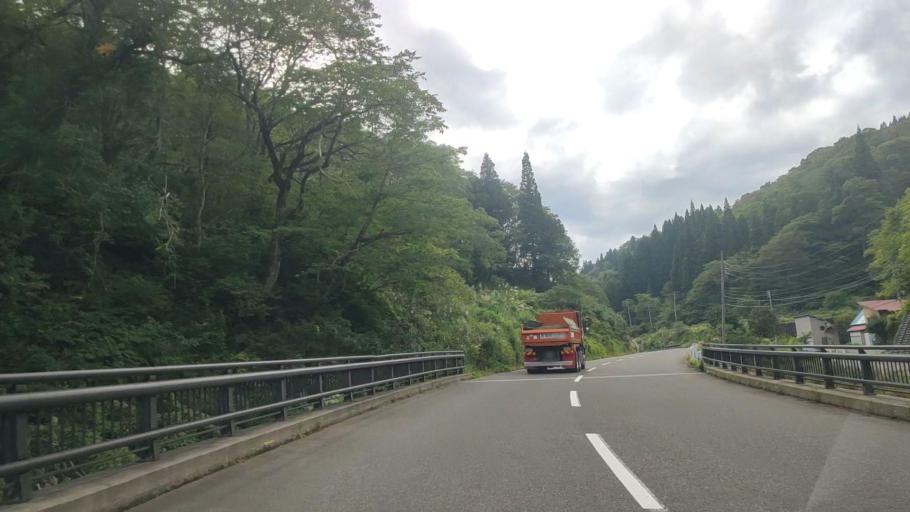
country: JP
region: Nagano
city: Iiyama
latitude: 36.8958
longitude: 138.3213
